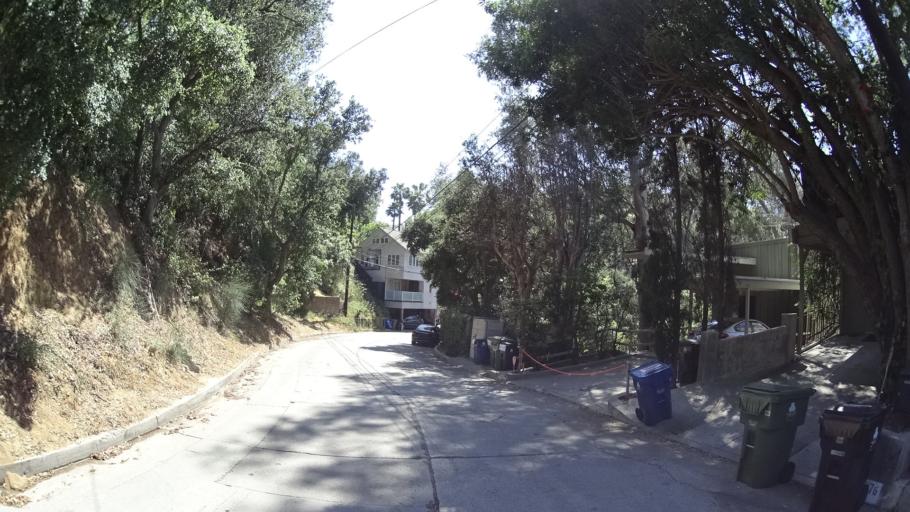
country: US
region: California
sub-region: Los Angeles County
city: West Hollywood
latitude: 34.1070
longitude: -118.3845
